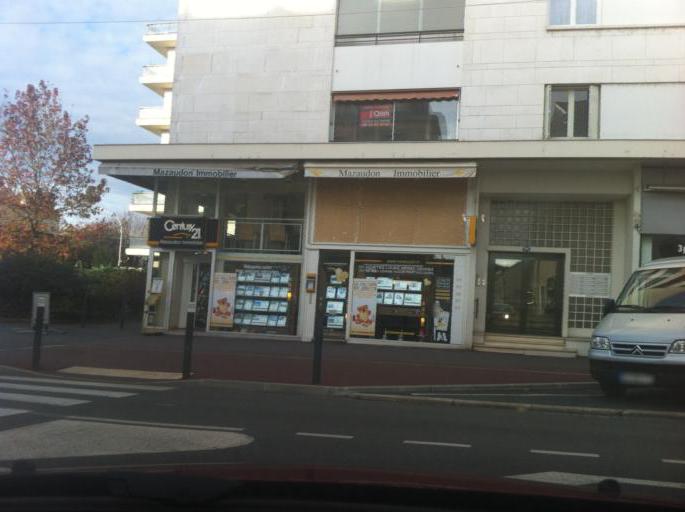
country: FR
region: Aquitaine
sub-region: Departement de la Dordogne
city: Perigueux
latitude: 45.1844
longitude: 0.7154
